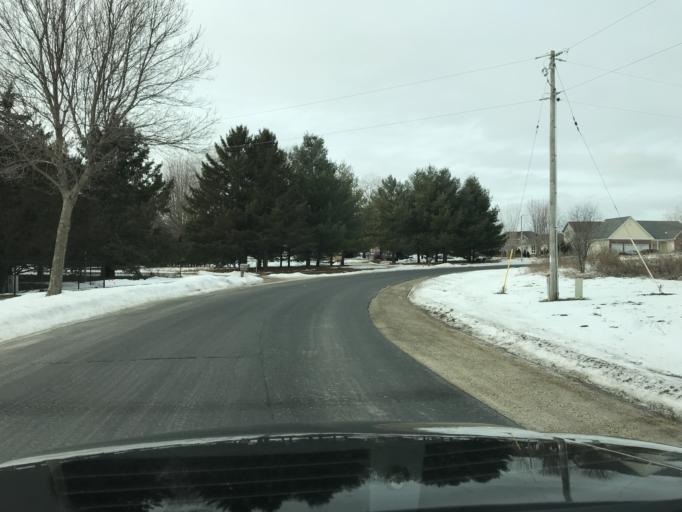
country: US
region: Wisconsin
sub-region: Dane County
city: Monona
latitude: 43.0936
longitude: -89.2696
